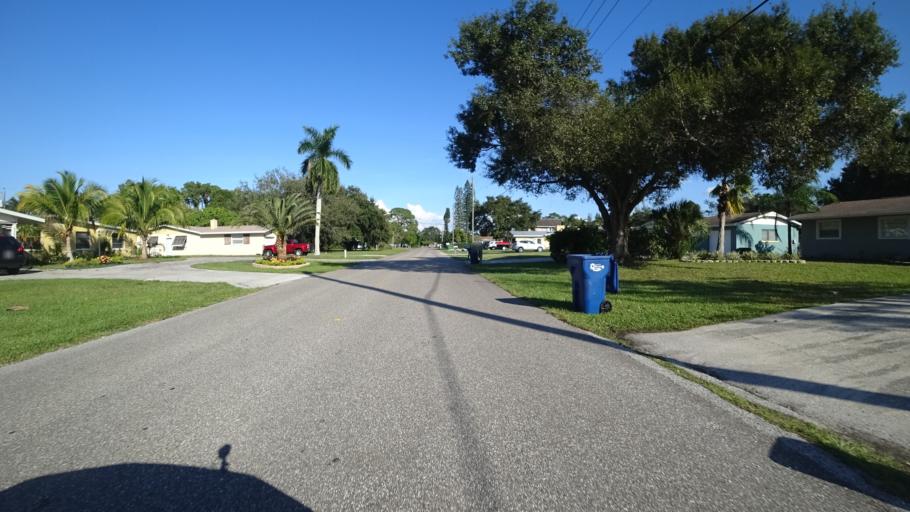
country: US
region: Florida
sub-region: Manatee County
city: West Bradenton
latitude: 27.4838
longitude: -82.6068
